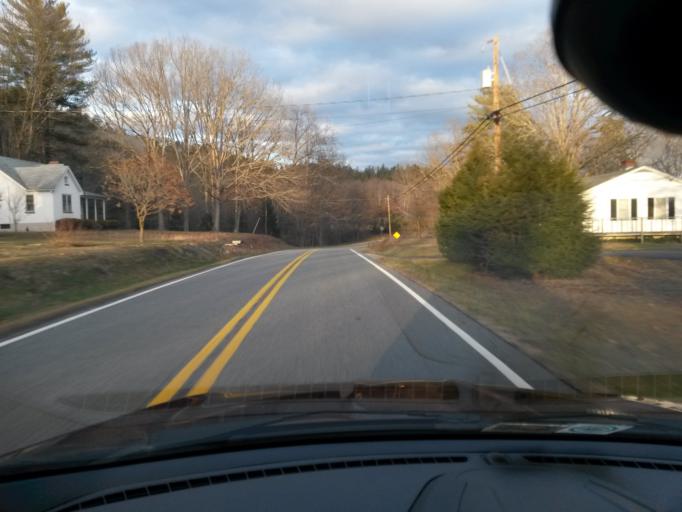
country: US
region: Virginia
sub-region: City of Covington
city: Covington
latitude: 37.7903
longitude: -80.0998
